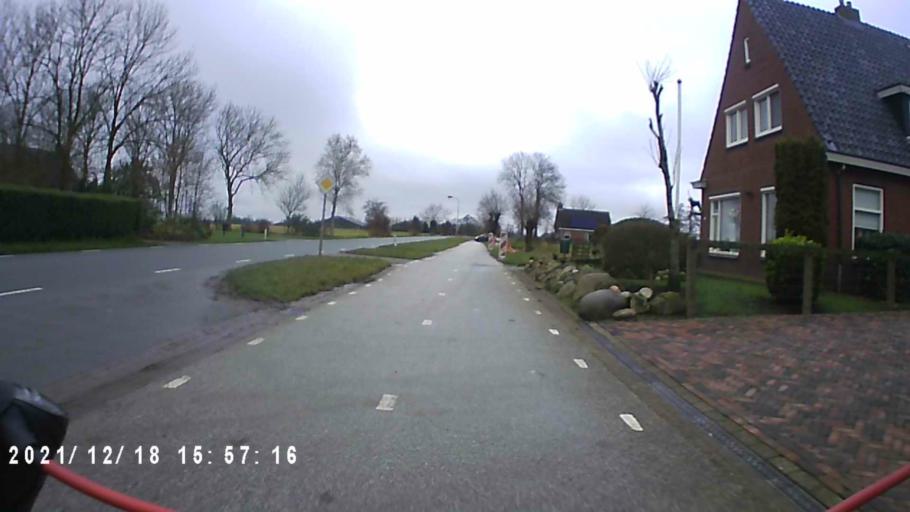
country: NL
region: Friesland
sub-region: Gemeente Dongeradeel
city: Anjum
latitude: 53.3341
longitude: 6.0959
